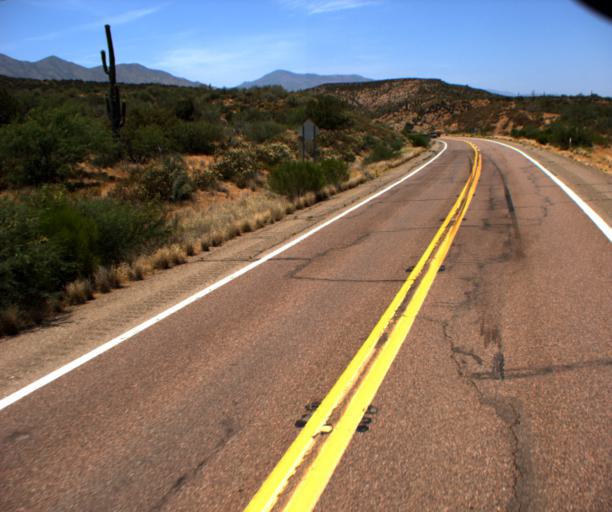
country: US
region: Arizona
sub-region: Gila County
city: Tonto Basin
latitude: 33.7992
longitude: -111.2696
